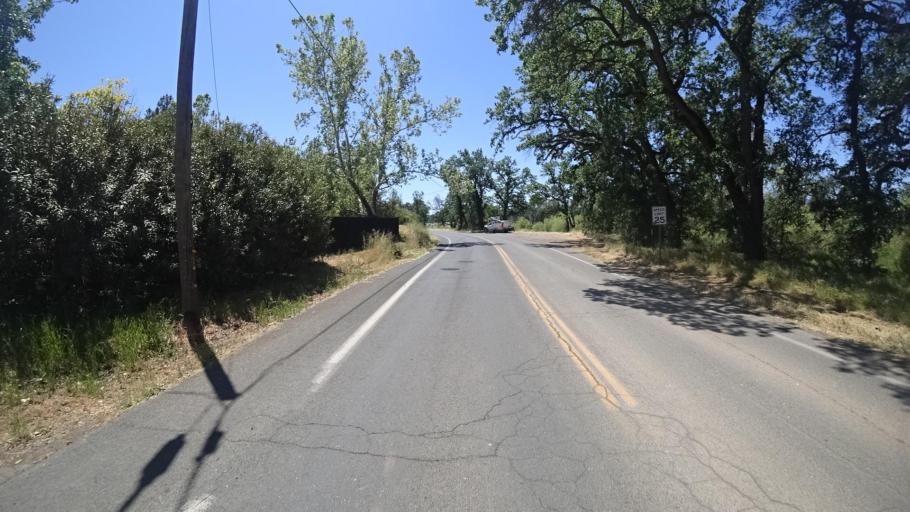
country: US
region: California
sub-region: Lake County
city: Lower Lake
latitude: 38.9208
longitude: -122.6118
